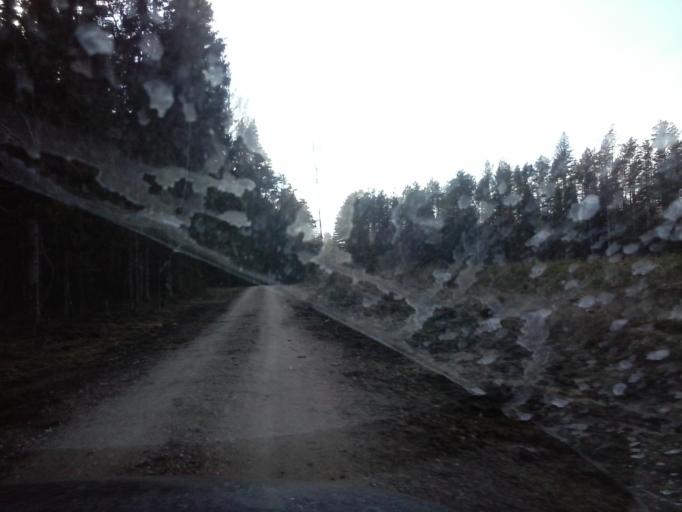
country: EE
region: Tartu
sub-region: Puhja vald
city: Puhja
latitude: 58.1591
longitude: 26.1470
